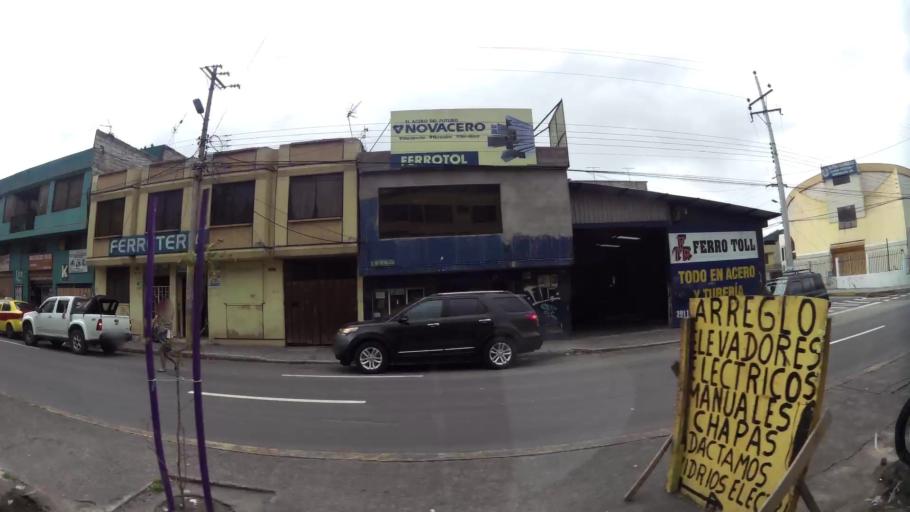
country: EC
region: Pichincha
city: Quito
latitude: -0.2745
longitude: -78.5408
